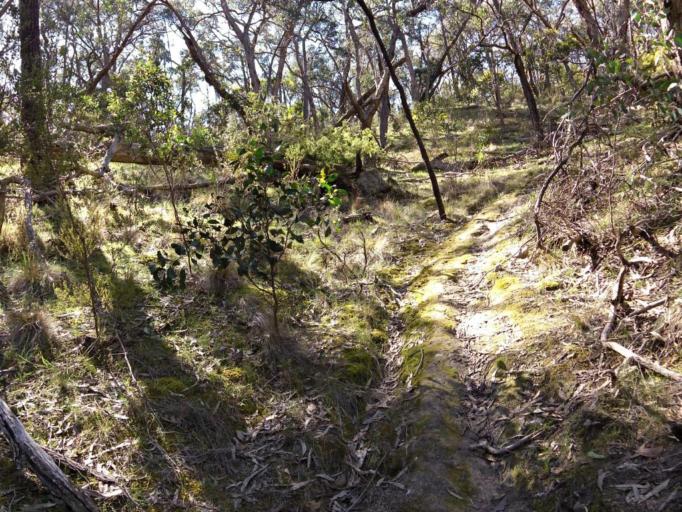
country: AU
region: Victoria
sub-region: Moorabool
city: Bacchus Marsh
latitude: -37.6610
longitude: 144.3180
